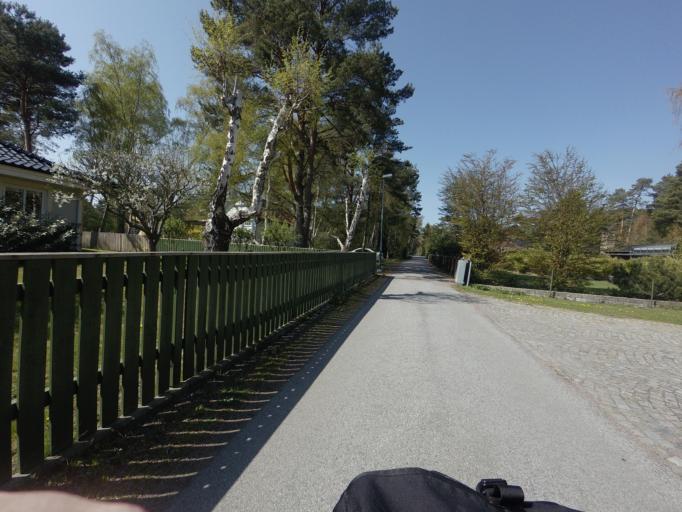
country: SE
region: Skane
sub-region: Vellinge Kommun
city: Hollviken
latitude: 55.4035
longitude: 12.9550
